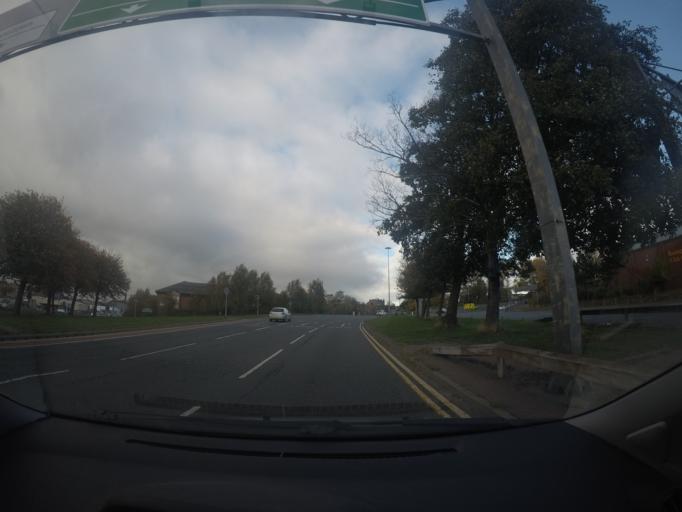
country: GB
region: England
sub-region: City and Borough of Leeds
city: Leeds
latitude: 53.8098
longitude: -1.5352
